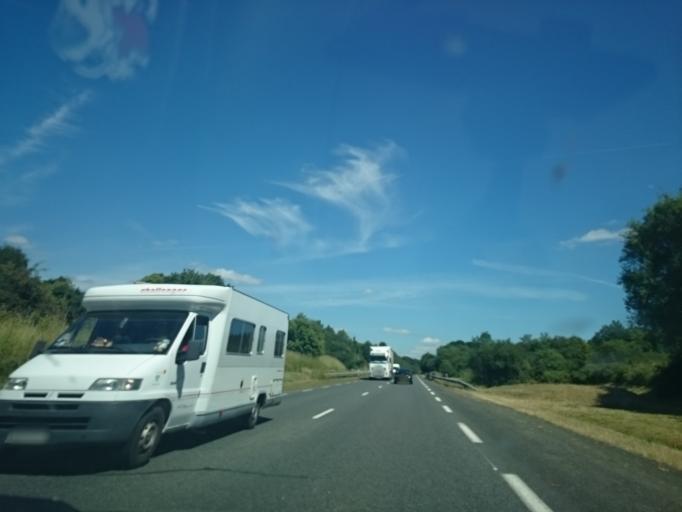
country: FR
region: Brittany
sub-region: Departement des Cotes-d'Armor
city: Plouguernevel
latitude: 48.2446
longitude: -3.2465
